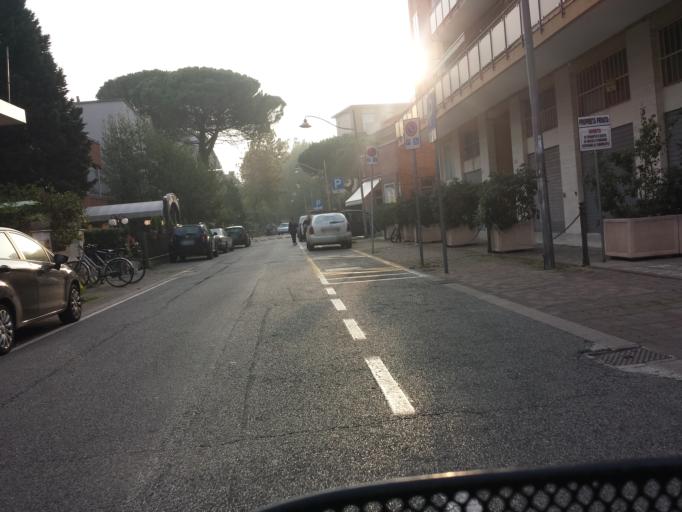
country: IT
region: Emilia-Romagna
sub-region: Provincia di Rimini
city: Rimini
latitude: 44.0677
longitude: 12.5771
